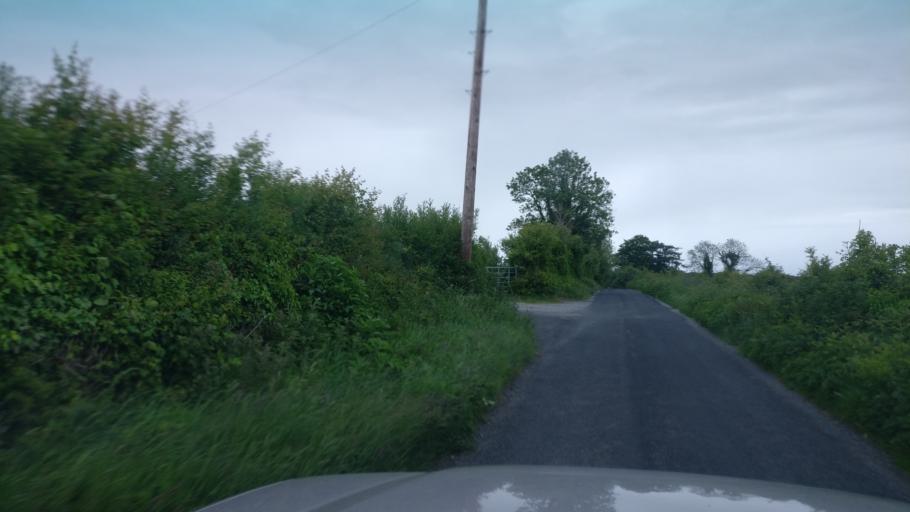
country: IE
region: Connaught
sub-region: County Galway
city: Loughrea
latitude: 53.1243
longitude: -8.4268
